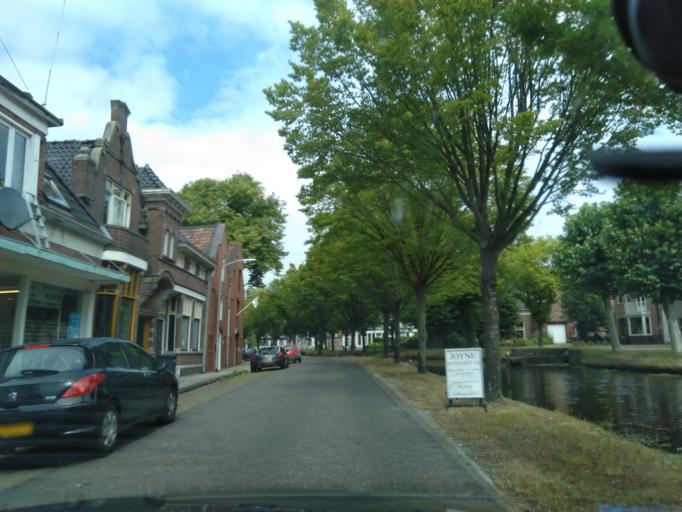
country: NL
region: Groningen
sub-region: Gemeente Pekela
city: Oude Pekela
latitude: 53.1037
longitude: 7.0119
